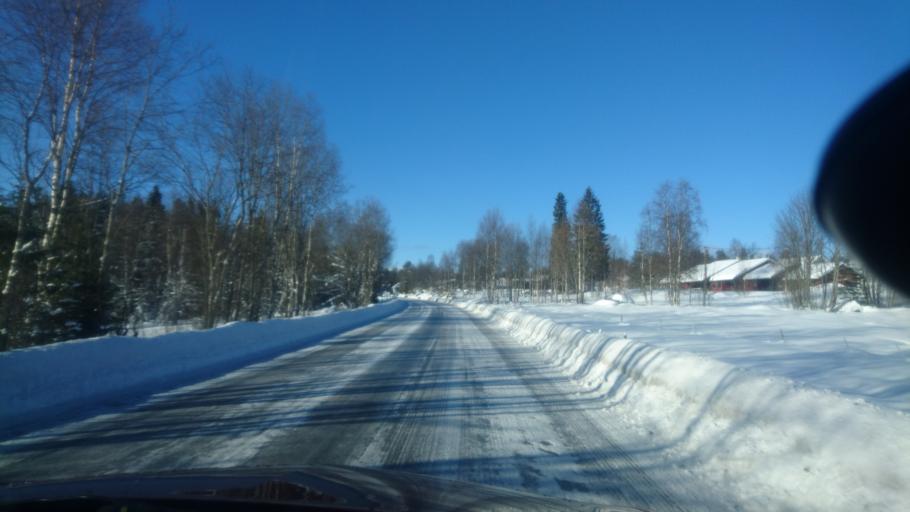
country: NO
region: Hedmark
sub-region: Trysil
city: Innbygda
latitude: 61.2535
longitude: 12.5307
